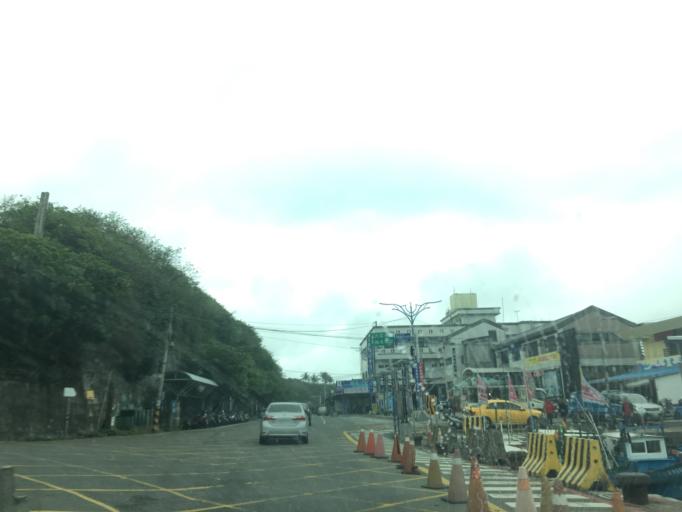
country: TW
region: Taiwan
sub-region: Taitung
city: Taitung
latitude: 22.7916
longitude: 121.1921
